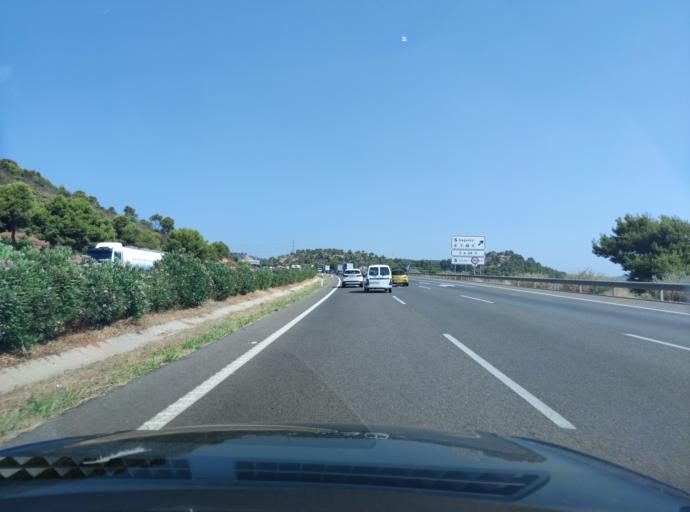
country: ES
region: Valencia
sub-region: Provincia de Valencia
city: Pucol
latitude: 39.6455
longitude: -0.3000
